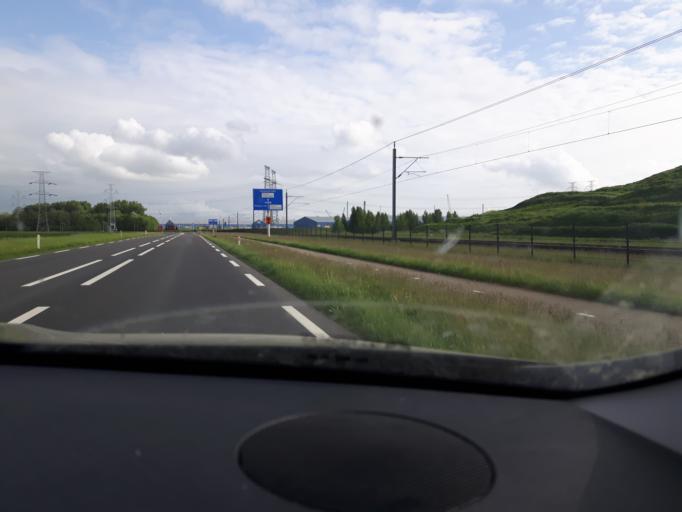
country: NL
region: Zeeland
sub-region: Gemeente Borsele
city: Borssele
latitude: 51.4661
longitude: 3.7272
